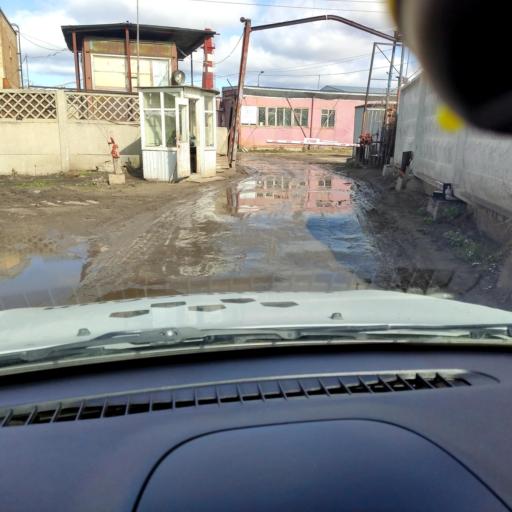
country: RU
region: Samara
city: Tol'yatti
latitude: 53.5615
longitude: 49.3181
